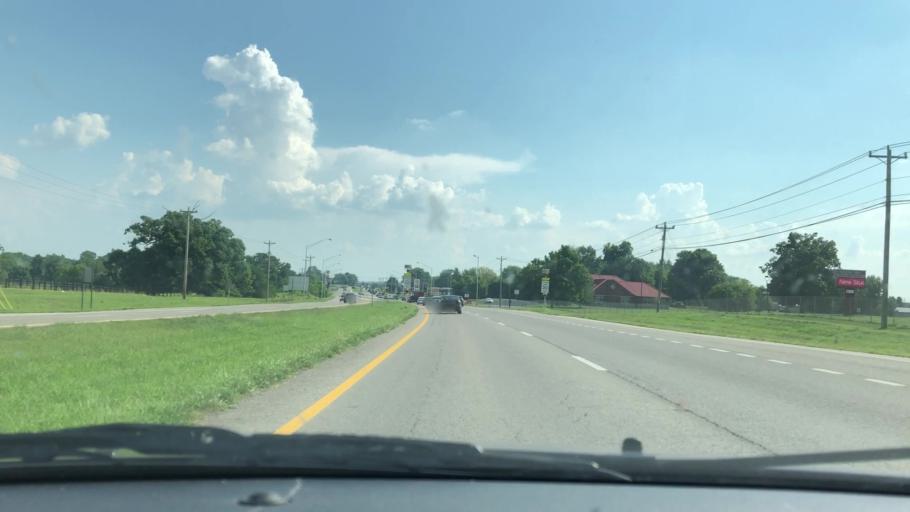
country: US
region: Tennessee
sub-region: Maury County
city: Spring Hill
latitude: 35.7157
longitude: -86.9718
